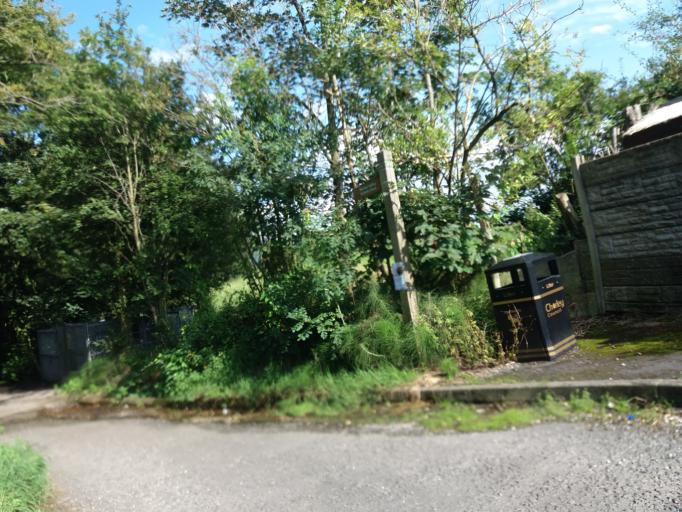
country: GB
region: England
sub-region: Lancashire
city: Coppull
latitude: 53.6259
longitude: -2.6507
